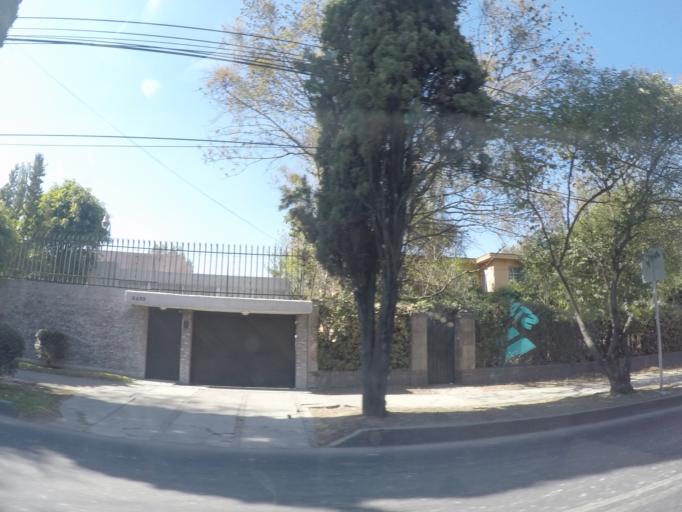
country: MX
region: Mexico City
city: Col. Bosques de las Lomas
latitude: 19.3997
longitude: -99.2340
